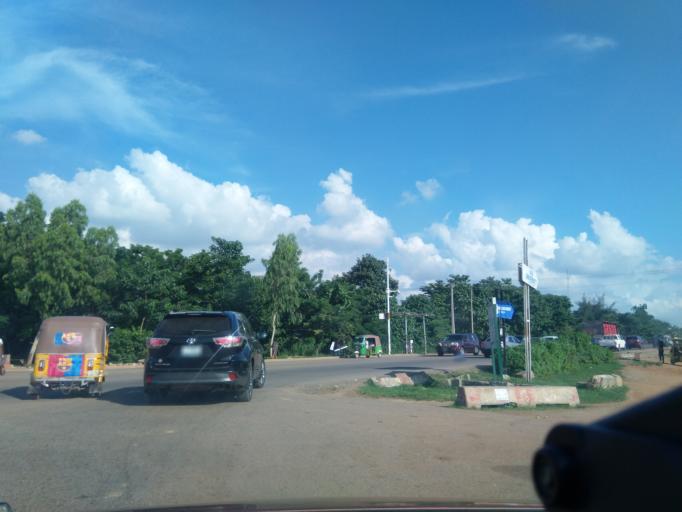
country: NG
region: Abuja Federal Capital Territory
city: Abuja
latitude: 9.0637
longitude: 7.4103
